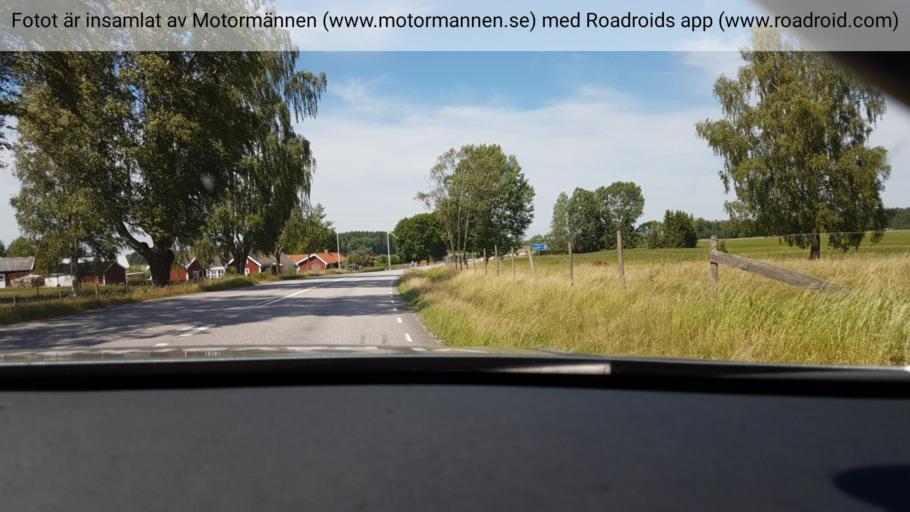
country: SE
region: Vaestra Goetaland
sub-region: Skovde Kommun
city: Stopen
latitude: 58.4704
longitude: 13.9557
